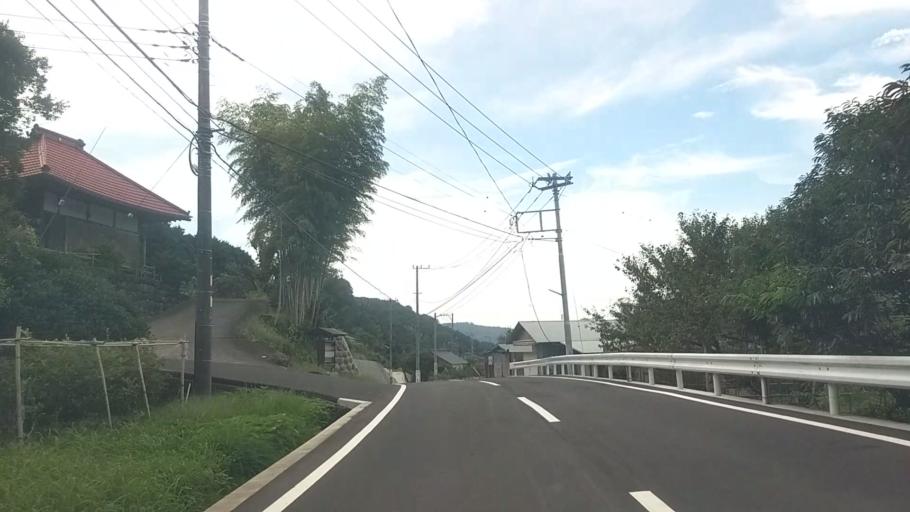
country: JP
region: Shizuoka
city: Ito
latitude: 34.9660
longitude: 138.9717
